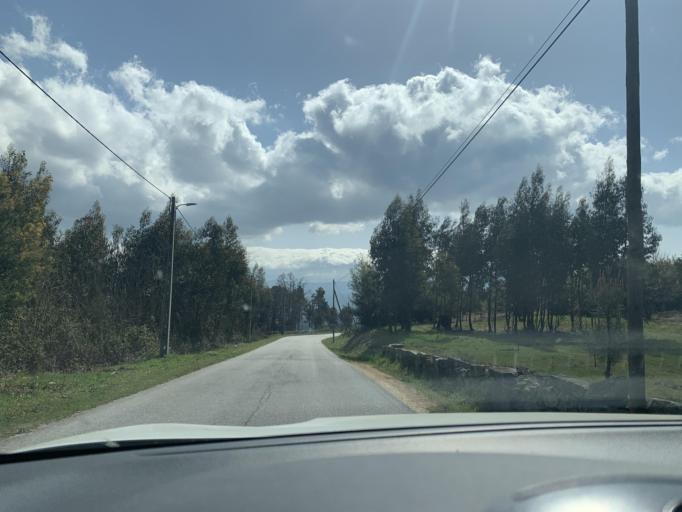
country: PT
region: Guarda
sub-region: Fornos de Algodres
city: Fornos de Algodres
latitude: 40.6105
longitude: -7.6053
